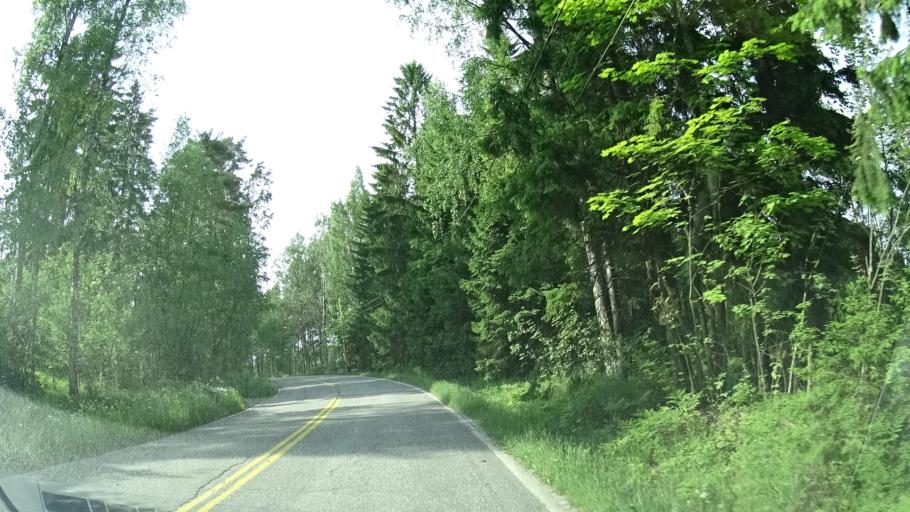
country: FI
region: Uusimaa
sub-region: Helsinki
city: Kirkkonummi
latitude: 60.0956
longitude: 24.5003
